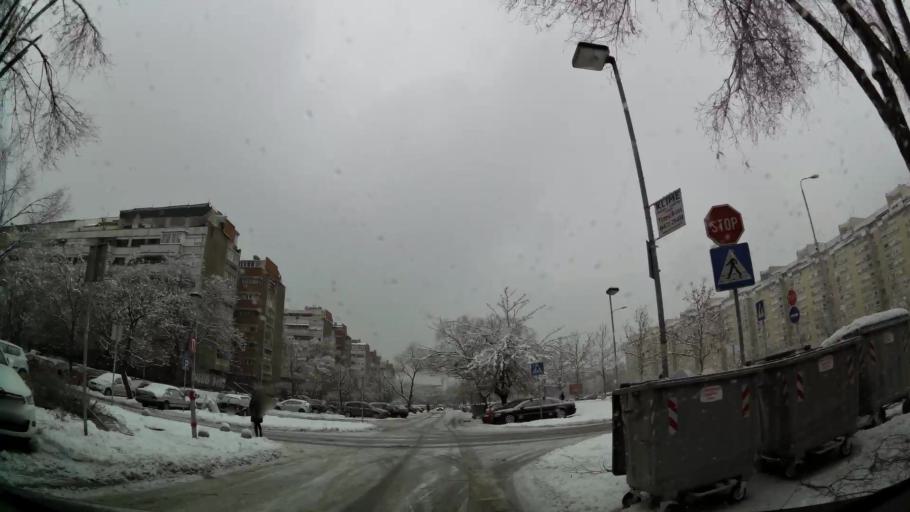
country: RS
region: Central Serbia
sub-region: Belgrade
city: Novi Beograd
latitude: 44.8173
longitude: 20.4179
